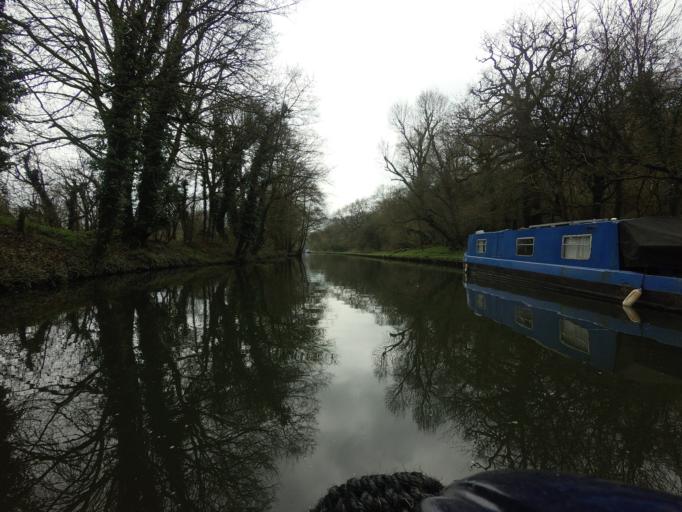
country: GB
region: England
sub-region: Hertfordshire
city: Watford
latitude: 51.6689
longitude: -0.4280
